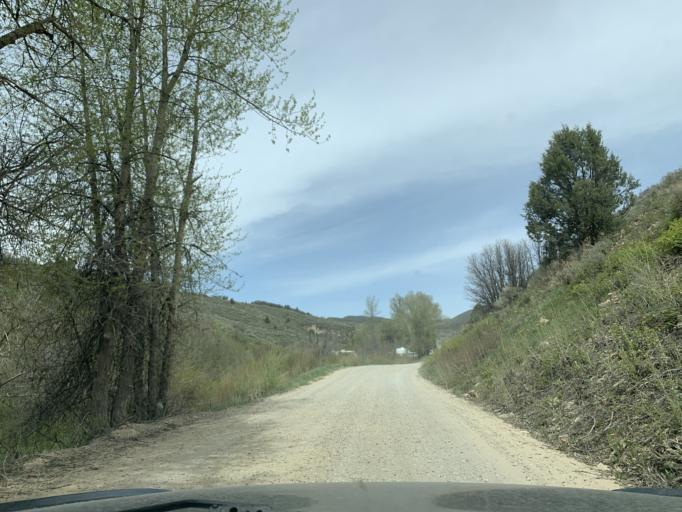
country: US
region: Utah
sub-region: Utah County
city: Mapleton
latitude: 40.1708
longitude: -111.3304
